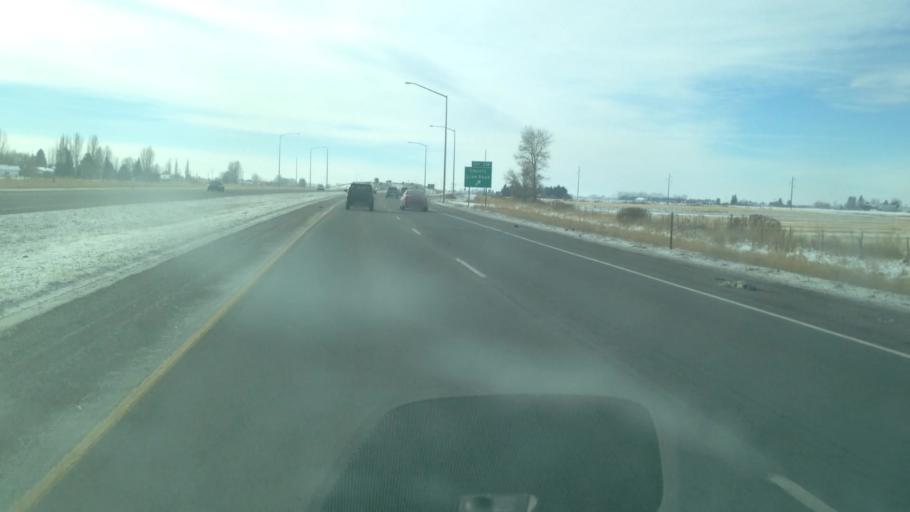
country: US
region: Idaho
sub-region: Bonneville County
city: Ucon
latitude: 43.6337
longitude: -111.9386
